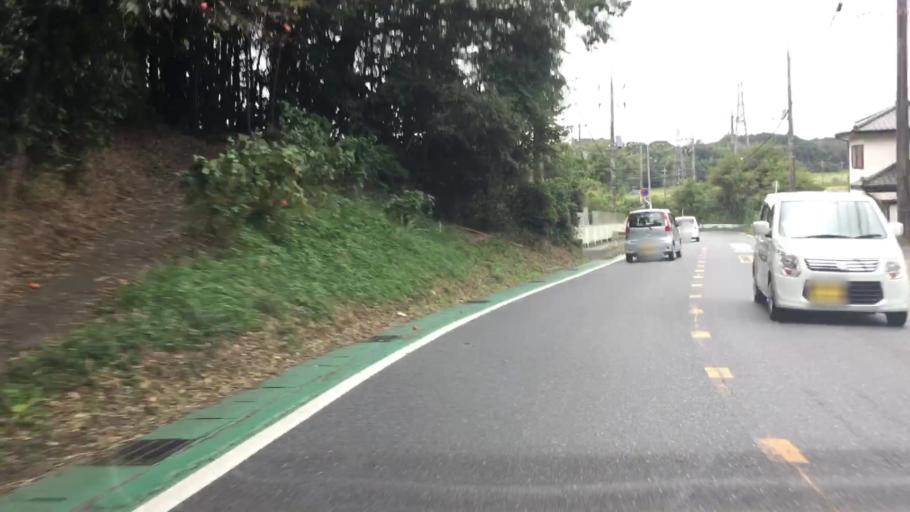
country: JP
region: Chiba
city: Shiroi
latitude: 35.8297
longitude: 140.1423
